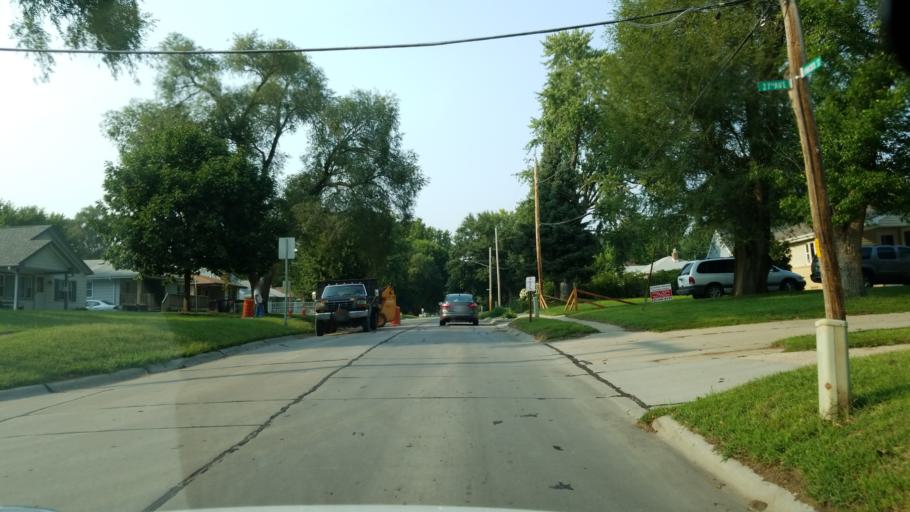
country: US
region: Nebraska
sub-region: Sarpy County
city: Bellevue
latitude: 41.1302
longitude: -95.8924
